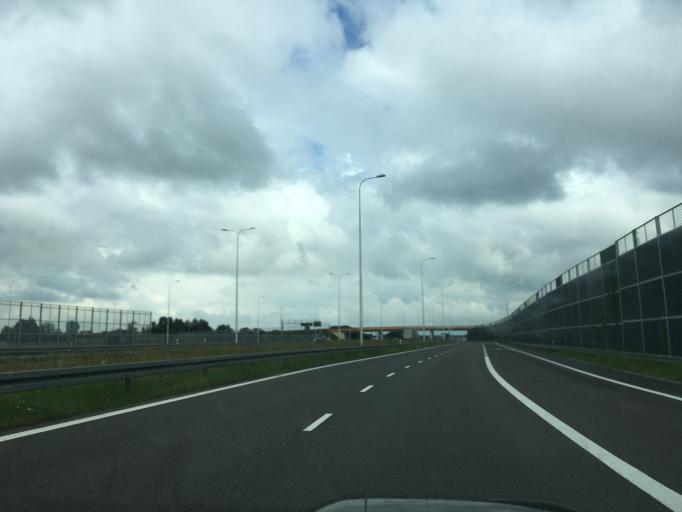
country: PL
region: Lublin Voivodeship
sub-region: Powiat lubelski
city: Jastkow
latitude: 51.2865
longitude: 22.4576
